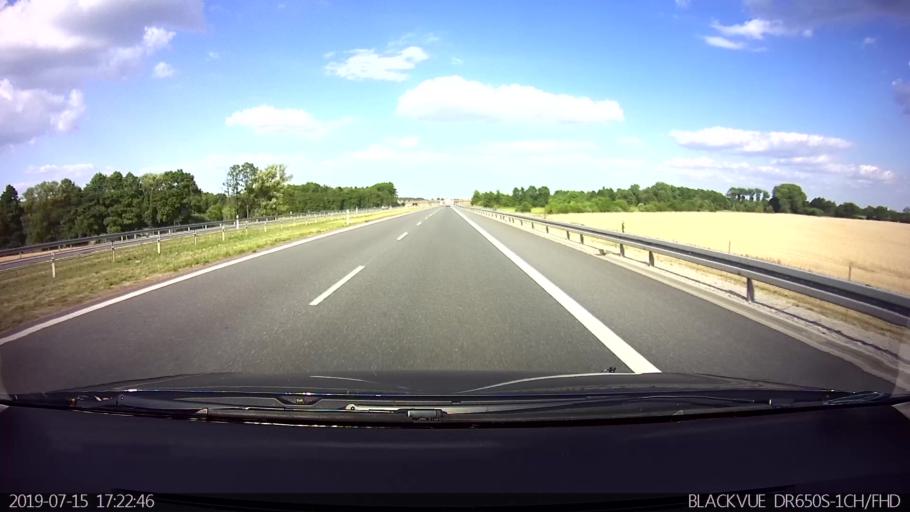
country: PL
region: Greater Poland Voivodeship
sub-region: Powiat kepinski
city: Kepno
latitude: 51.3169
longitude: 17.9670
